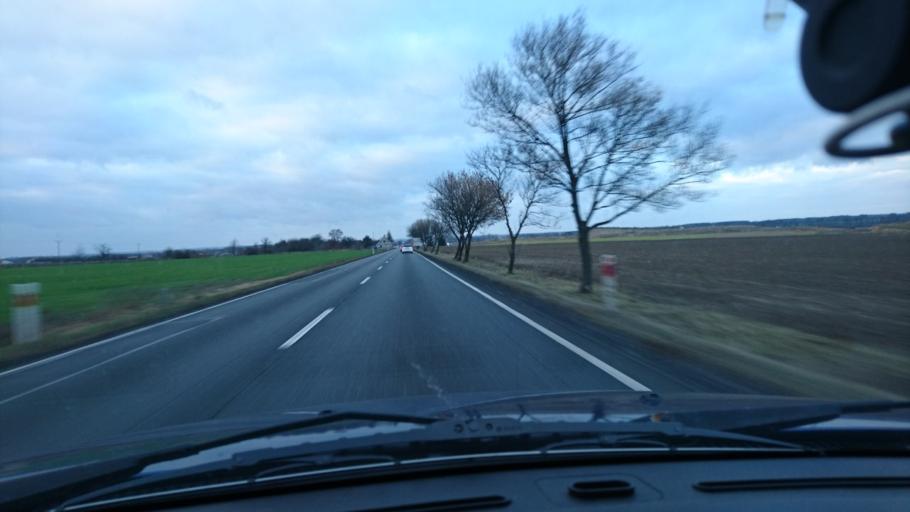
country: PL
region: Greater Poland Voivodeship
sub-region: Powiat kepinski
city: Baranow
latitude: 51.2517
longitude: 18.0141
